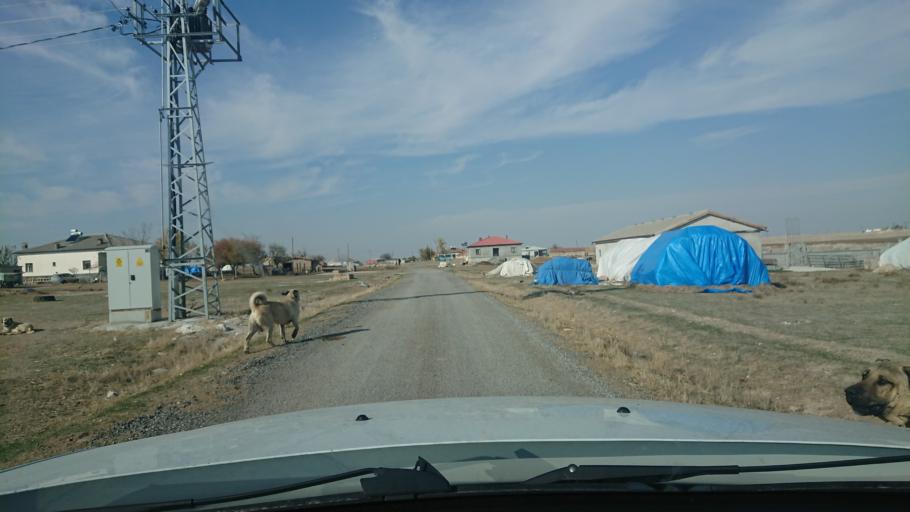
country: TR
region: Aksaray
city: Sultanhani
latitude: 38.2555
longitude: 33.4791
